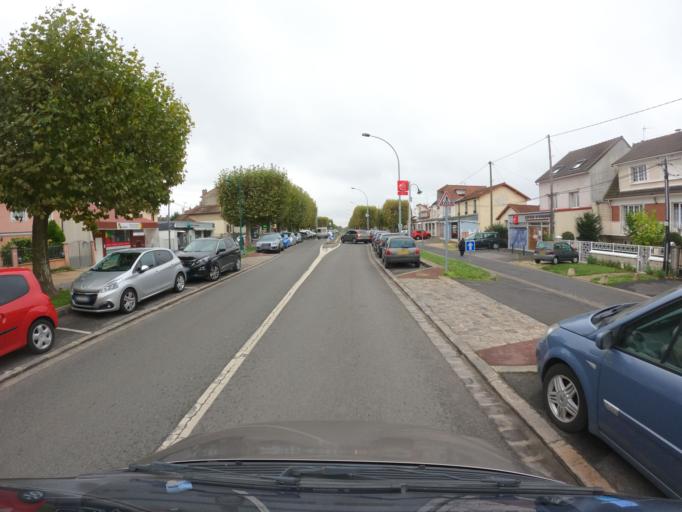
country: FR
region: Ile-de-France
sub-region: Departement du Val-de-Marne
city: Chennevieres-sur-Marne
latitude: 48.7908
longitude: 2.5339
